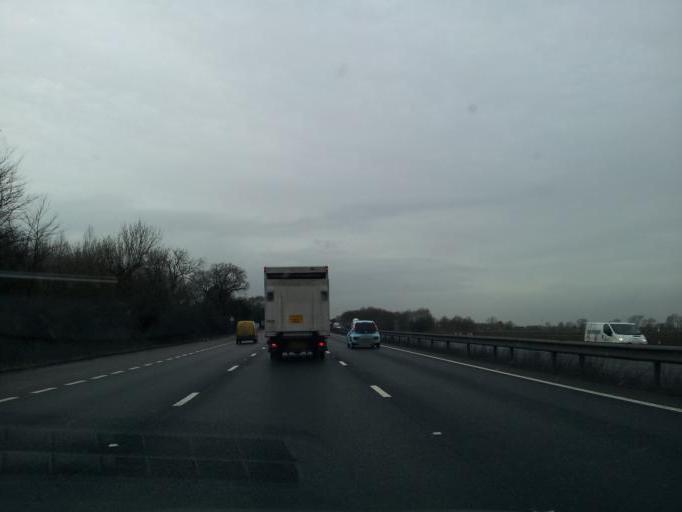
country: GB
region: England
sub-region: Cambridgeshire
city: Girton
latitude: 52.2446
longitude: 0.0498
